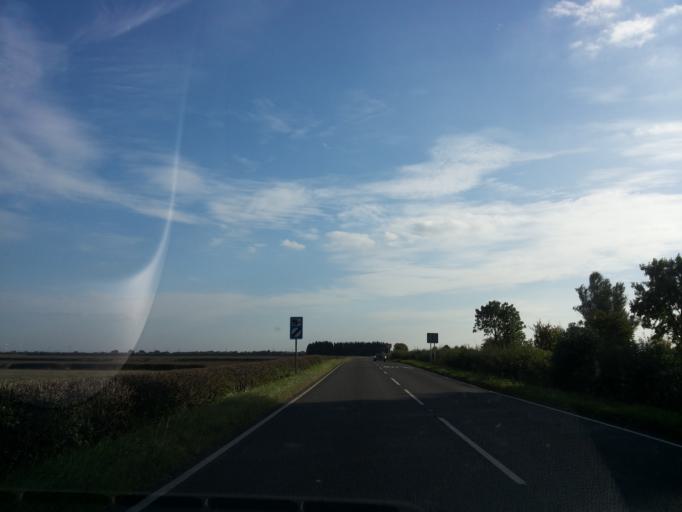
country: GB
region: England
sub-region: East Riding of Yorkshire
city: Rawcliffe
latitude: 53.6543
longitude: -0.9898
